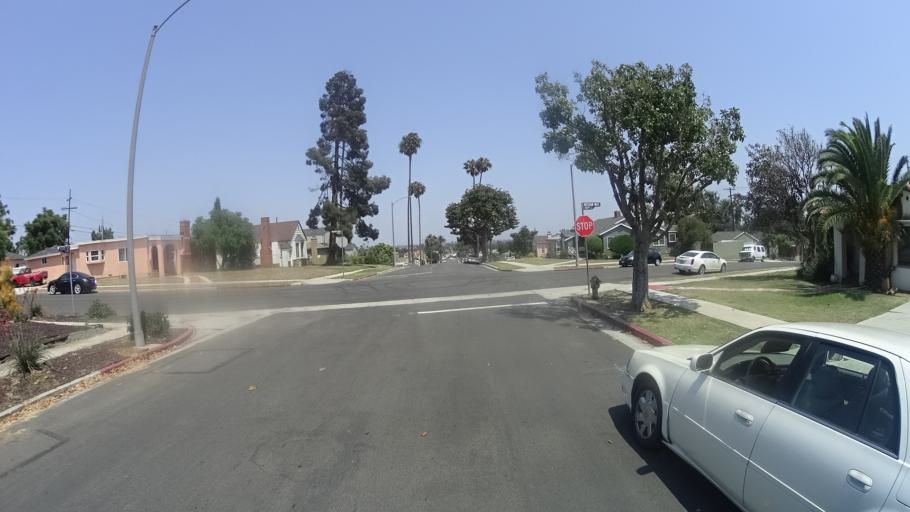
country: US
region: California
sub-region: Los Angeles County
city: View Park-Windsor Hills
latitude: 33.9826
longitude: -118.3480
